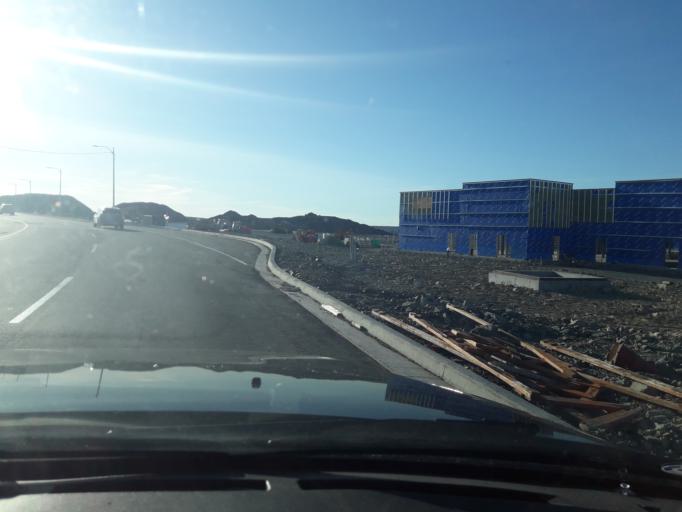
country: CA
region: Newfoundland and Labrador
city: Mount Pearl
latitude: 47.5101
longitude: -52.8521
